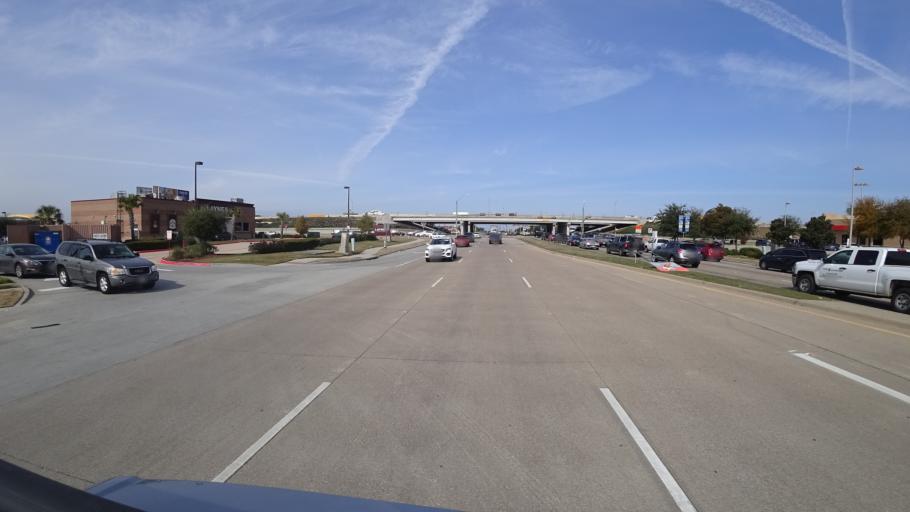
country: US
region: Texas
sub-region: Denton County
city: The Colony
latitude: 33.0644
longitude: -96.8882
